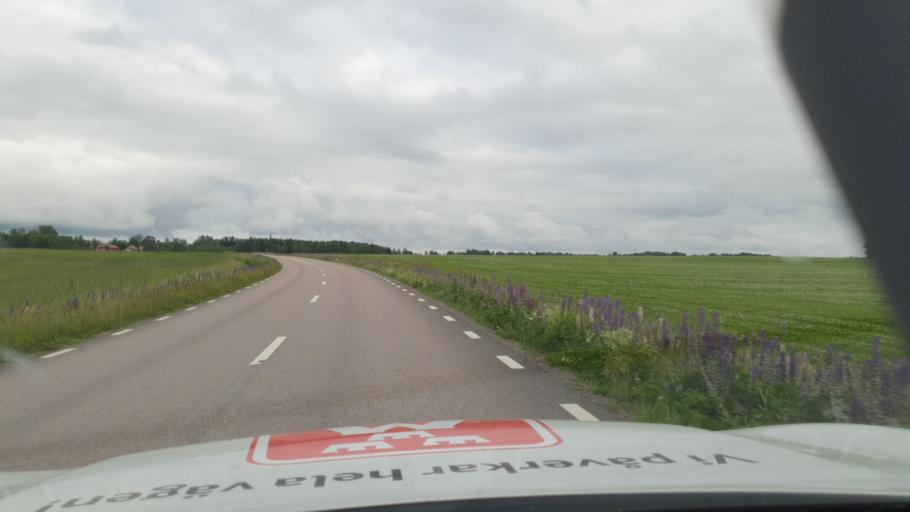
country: SE
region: Vaermland
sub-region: Kils Kommun
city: Kil
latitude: 59.5385
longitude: 13.3001
